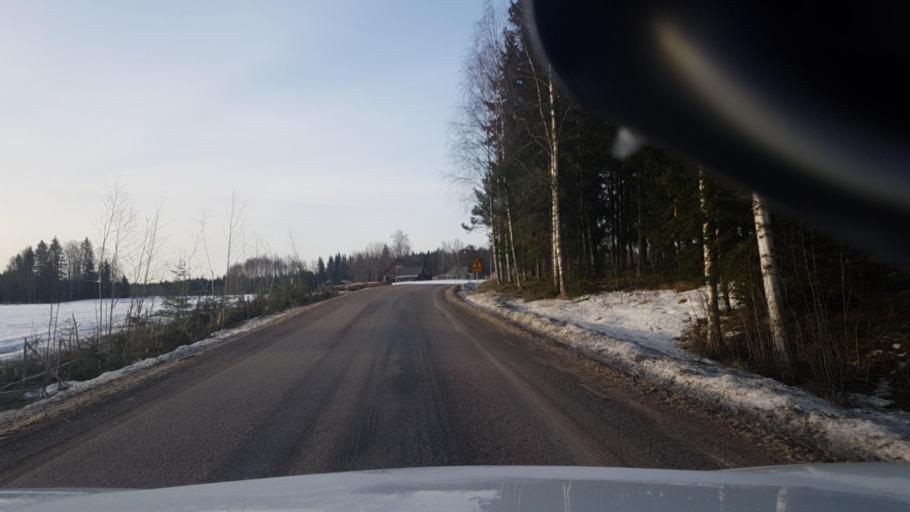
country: SE
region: Vaermland
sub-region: Eda Kommun
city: Charlottenberg
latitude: 59.8713
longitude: 12.3491
